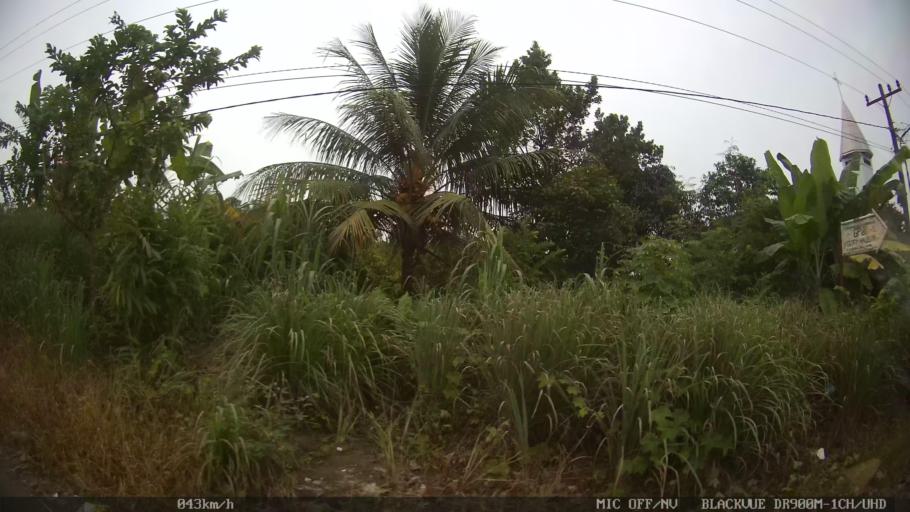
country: ID
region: North Sumatra
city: Deli Tua
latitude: 3.5392
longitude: 98.7350
